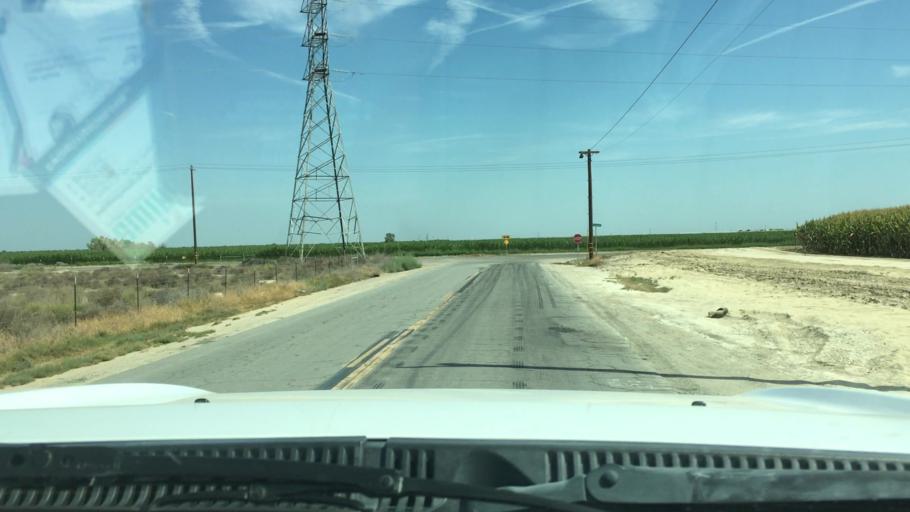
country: US
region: California
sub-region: Kern County
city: Buttonwillow
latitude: 35.4413
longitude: -119.3759
